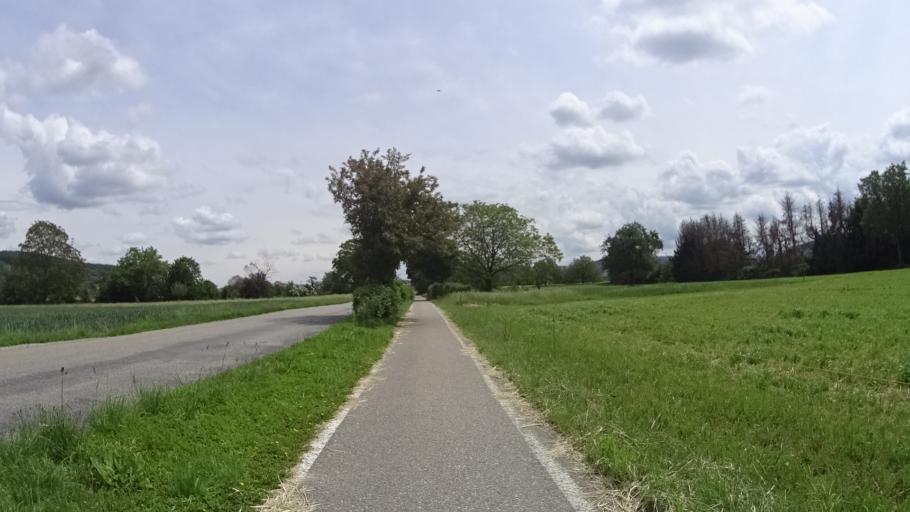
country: DE
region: Baden-Wuerttemberg
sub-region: Freiburg Region
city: Grenzach-Wyhlen
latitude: 47.5468
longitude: 7.6756
